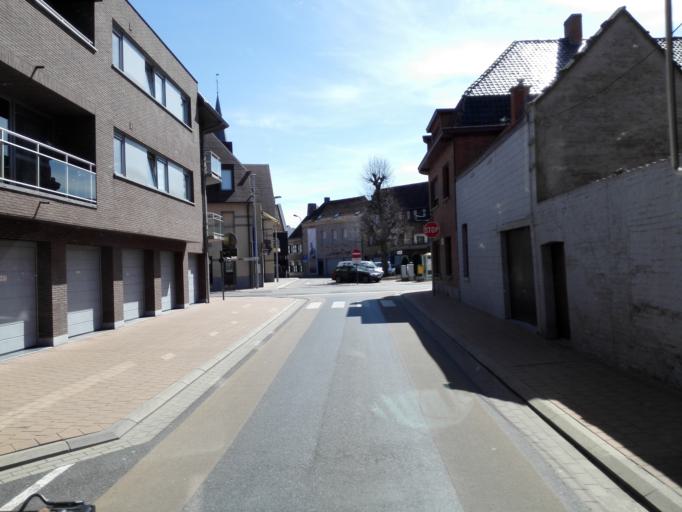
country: BE
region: Flanders
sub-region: Provincie West-Vlaanderen
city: Meulebeke
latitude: 50.9511
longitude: 3.2869
